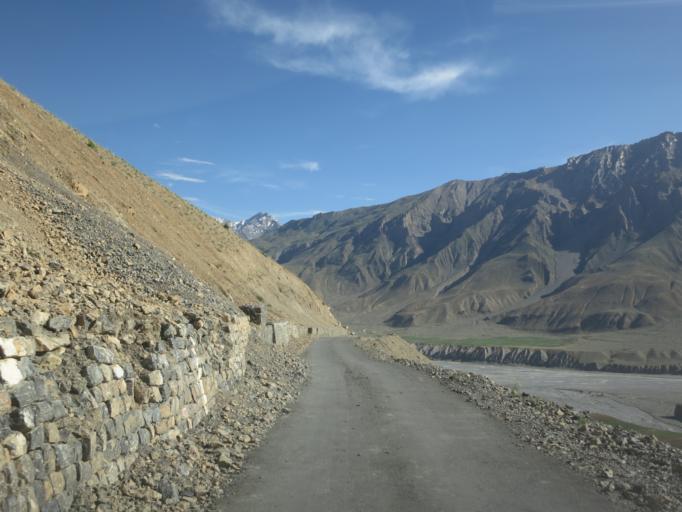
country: IN
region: Himachal Pradesh
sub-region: Shimla
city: Sarahan
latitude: 32.3109
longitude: 78.0031
